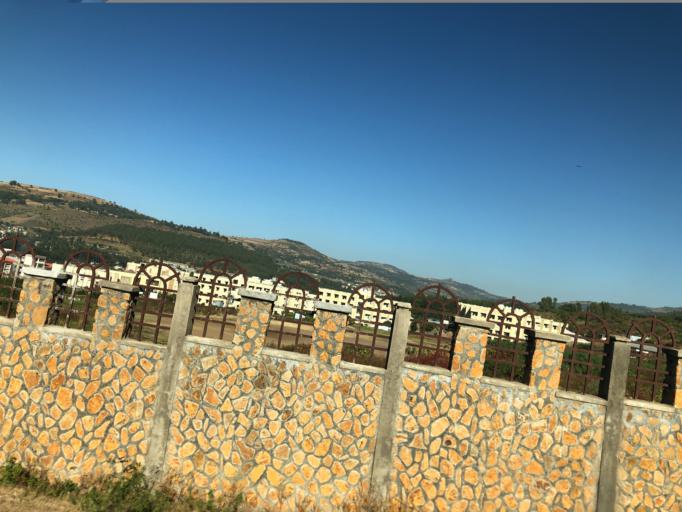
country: ET
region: Amhara
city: Gondar
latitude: 12.5749
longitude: 37.4464
